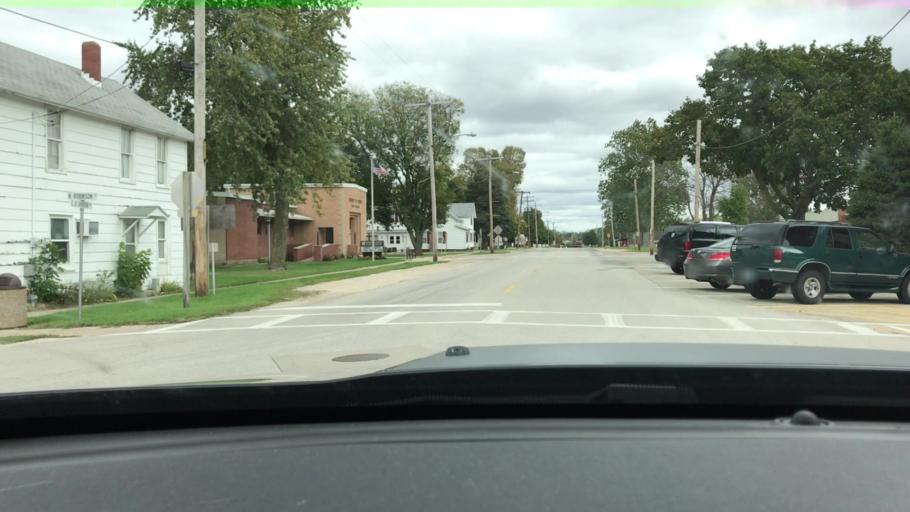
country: US
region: Illinois
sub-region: LaSalle County
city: Sheridan
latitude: 41.5299
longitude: -88.6801
